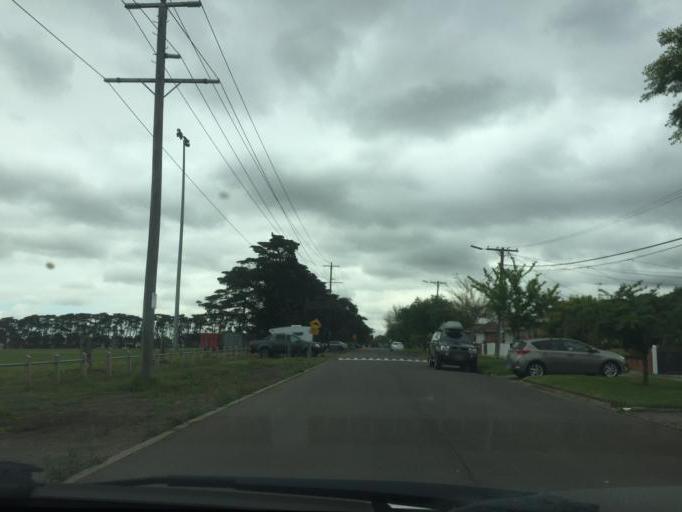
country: AU
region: Victoria
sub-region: Hobsons Bay
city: South Kingsville
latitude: -37.8184
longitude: 144.8708
